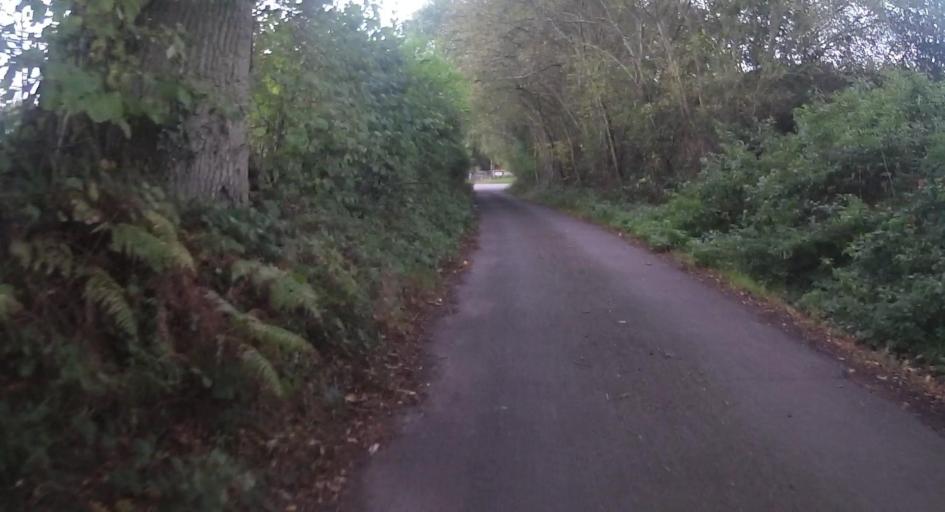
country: GB
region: England
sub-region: Hampshire
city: Hook
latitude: 51.3151
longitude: -0.9284
